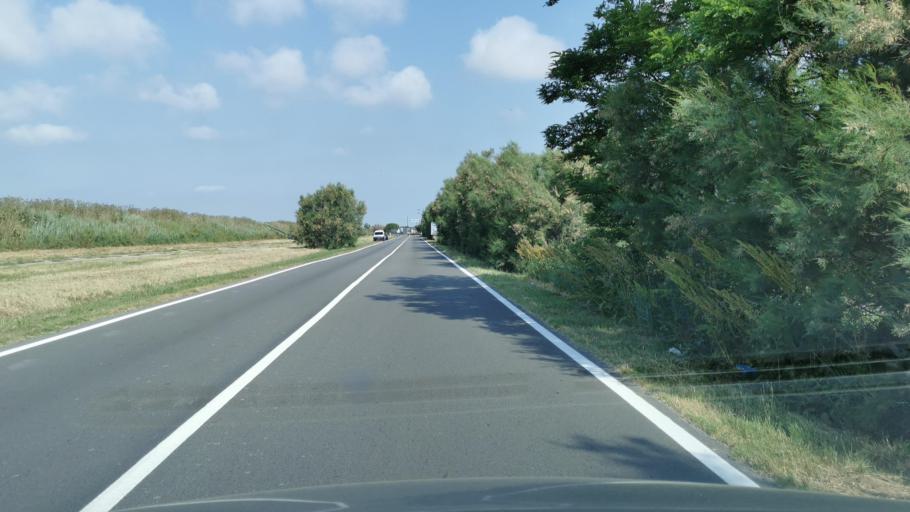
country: IT
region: Emilia-Romagna
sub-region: Provincia di Ferrara
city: Comacchio
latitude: 44.6823
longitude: 12.1991
